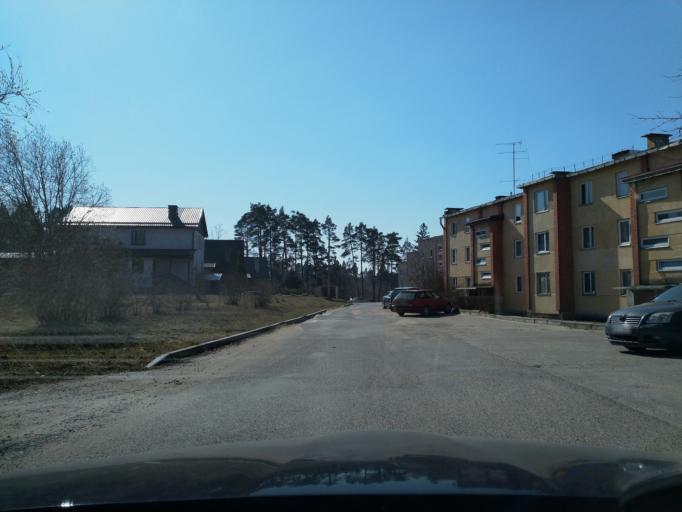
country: LV
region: Kuldigas Rajons
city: Kuldiga
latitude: 56.9643
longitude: 21.9275
